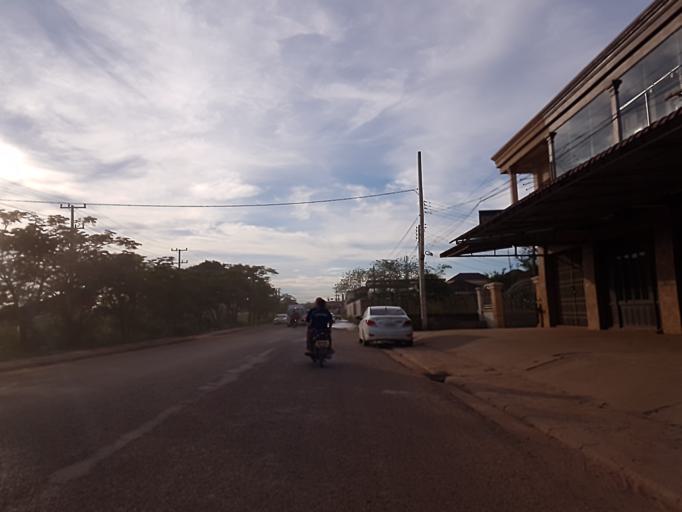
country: TH
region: Nong Khai
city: Si Chiang Mai
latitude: 18.0111
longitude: 102.5476
